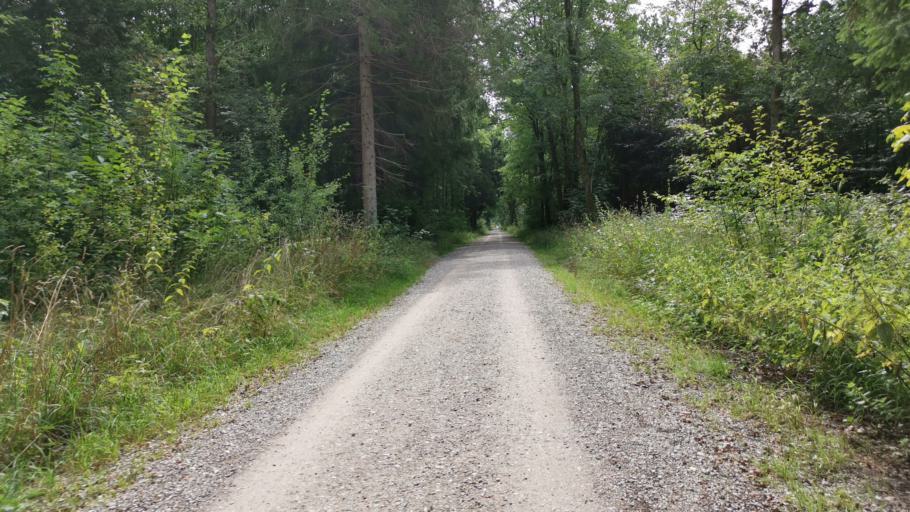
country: DE
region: Bavaria
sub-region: Upper Bavaria
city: Unterhaching
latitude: 48.0834
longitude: 11.5686
